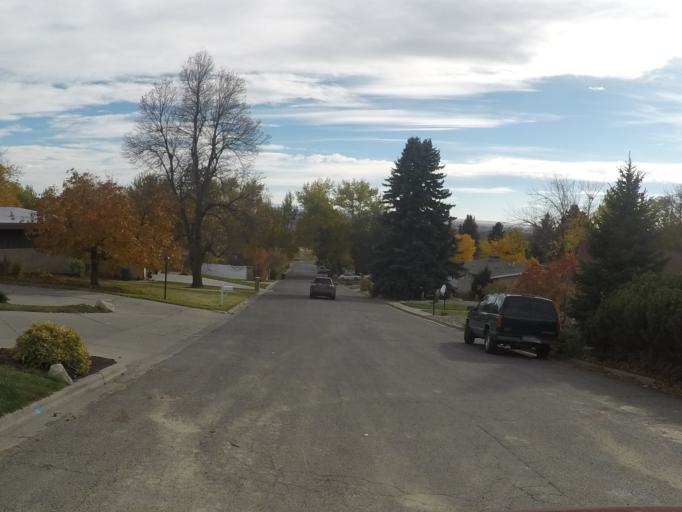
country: US
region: Montana
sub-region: Yellowstone County
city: Billings
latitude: 45.8013
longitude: -108.5564
